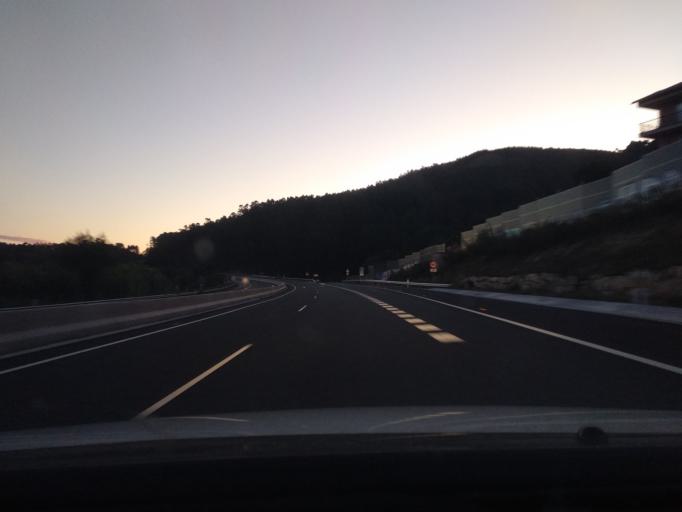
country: ES
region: Galicia
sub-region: Provincia de Pontevedra
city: Moana
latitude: 42.3070
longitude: -8.7406
